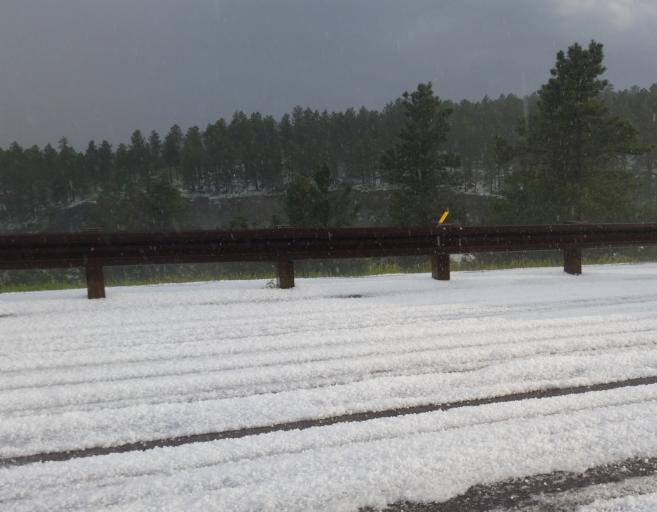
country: US
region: South Dakota
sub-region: Pennington County
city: Colonial Pine Hills
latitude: 43.9420
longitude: -103.3859
